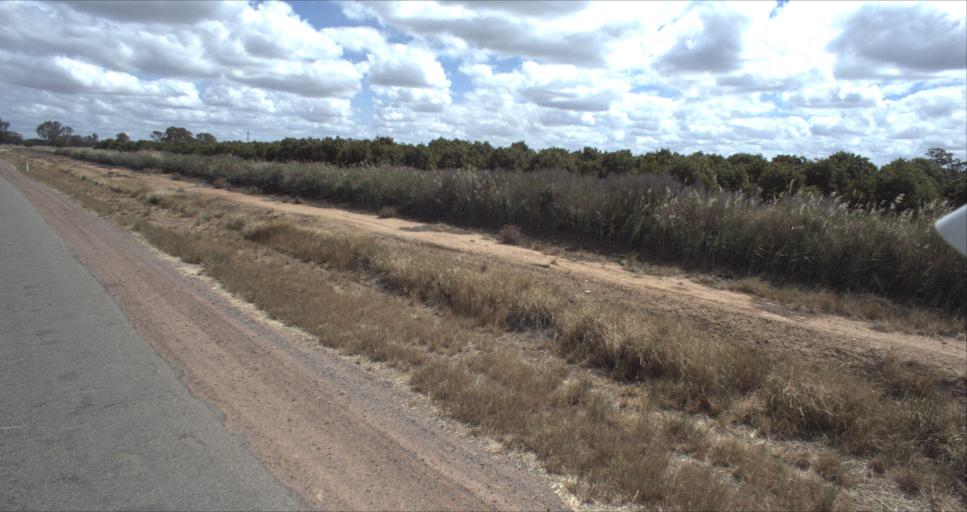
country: AU
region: New South Wales
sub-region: Leeton
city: Leeton
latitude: -34.5882
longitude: 146.3709
